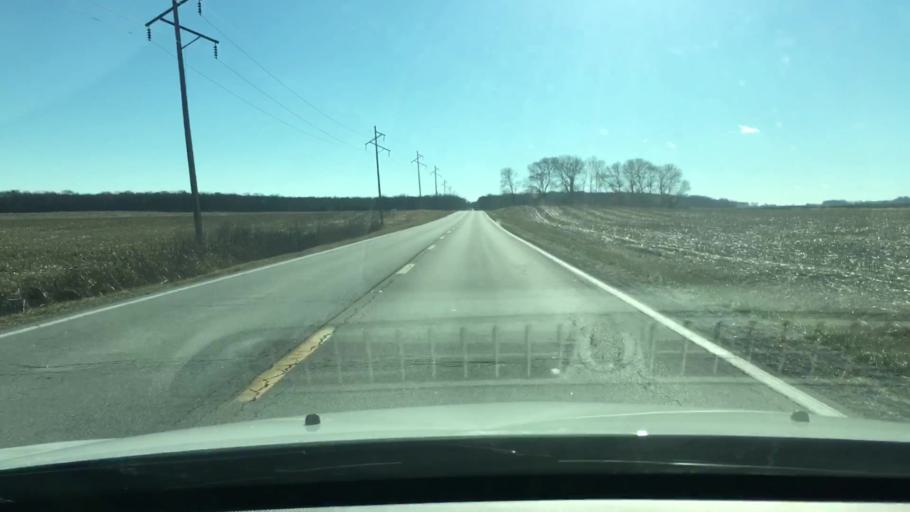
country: US
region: Illinois
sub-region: Morgan County
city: Meredosia
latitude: 39.9193
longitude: -90.4945
